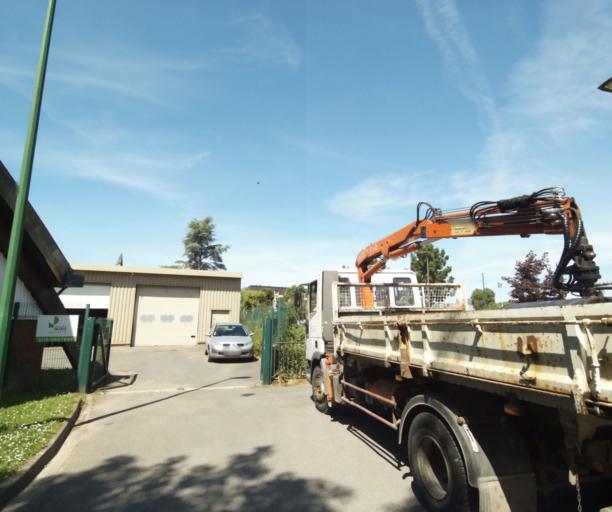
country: FR
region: Champagne-Ardenne
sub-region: Departement des Ardennes
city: Charleville-Mezieres
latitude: 49.7507
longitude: 4.7216
